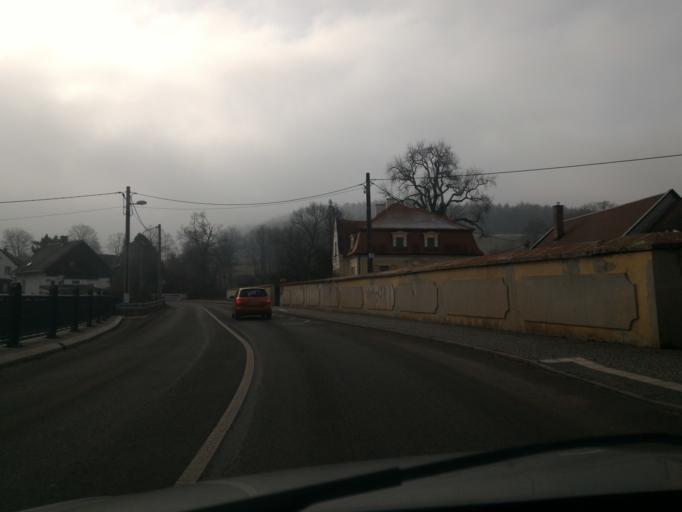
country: CZ
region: Liberecky
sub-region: Okres Liberec
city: Raspenava
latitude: 50.8992
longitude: 15.1367
